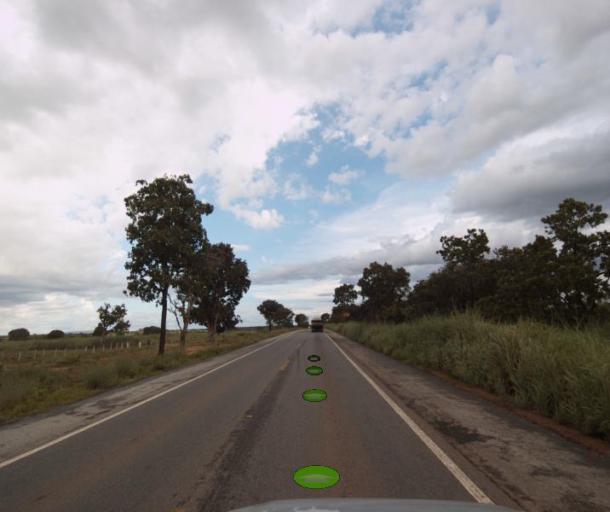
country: BR
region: Goias
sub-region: Porangatu
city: Porangatu
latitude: -13.3563
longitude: -49.1237
